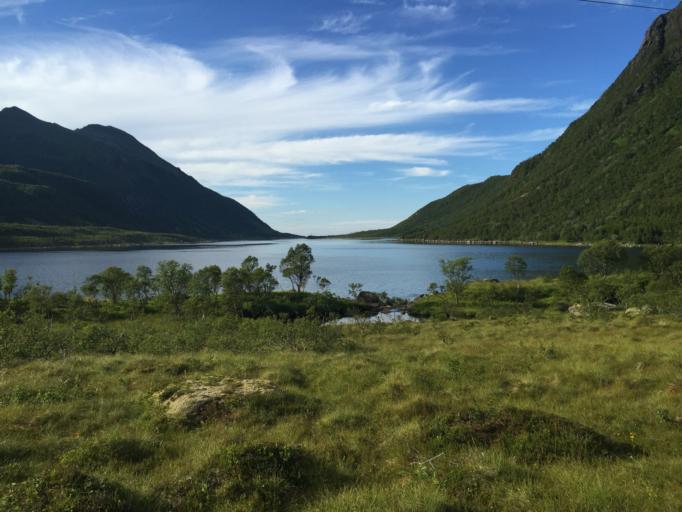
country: NO
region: Nordland
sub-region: Vagan
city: Kabelvag
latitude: 68.3003
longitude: 14.4306
